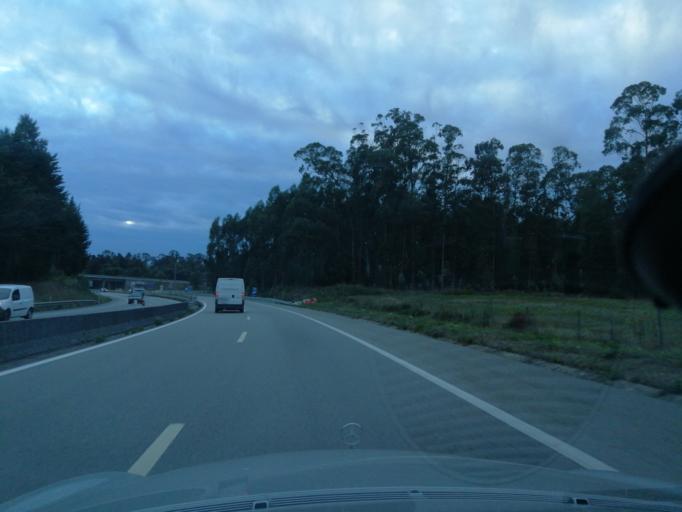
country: PT
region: Aveiro
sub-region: Albergaria-A-Velha
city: Albergaria-a-Velha
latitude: 40.6890
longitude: -8.5172
